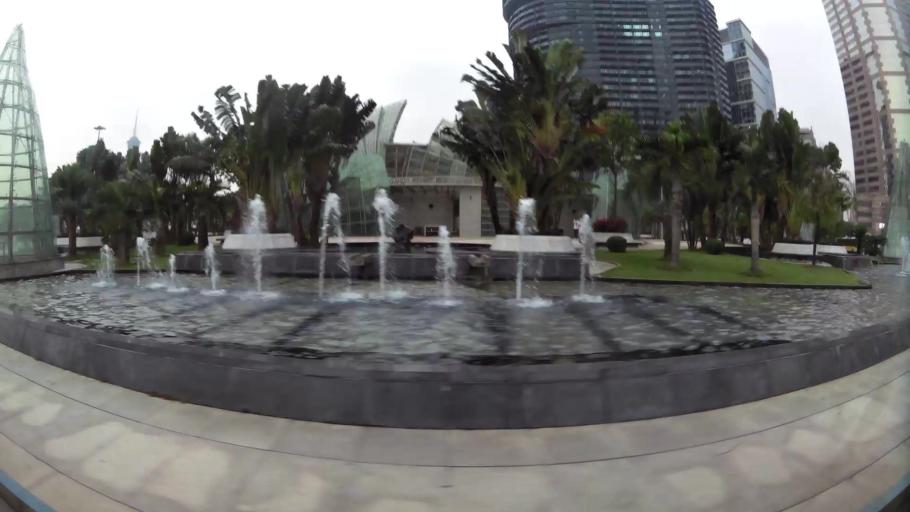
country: MO
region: Macau
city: Macau
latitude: 22.1885
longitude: 113.5440
